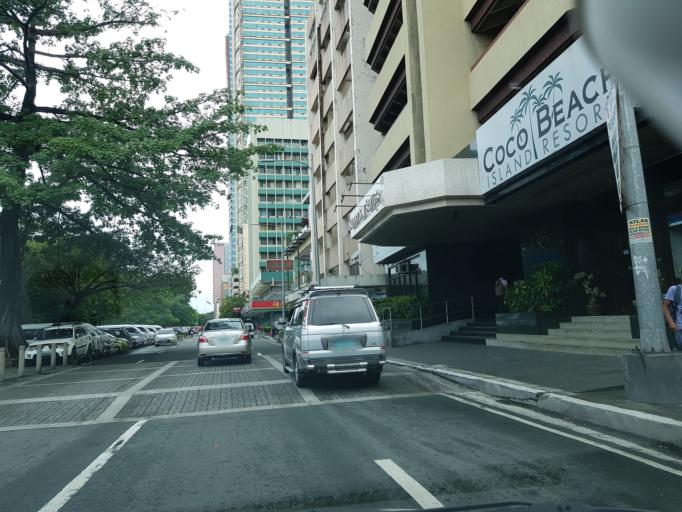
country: PH
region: Metro Manila
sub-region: City of Manila
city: Port Area
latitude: 14.5744
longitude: 120.9807
